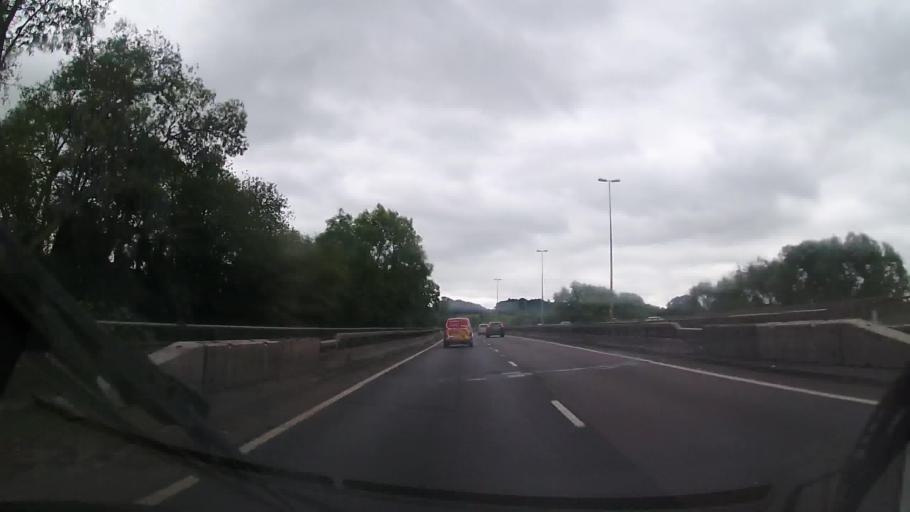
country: GB
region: England
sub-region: Staffordshire
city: Uttoxeter
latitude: 52.9076
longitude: -1.8449
